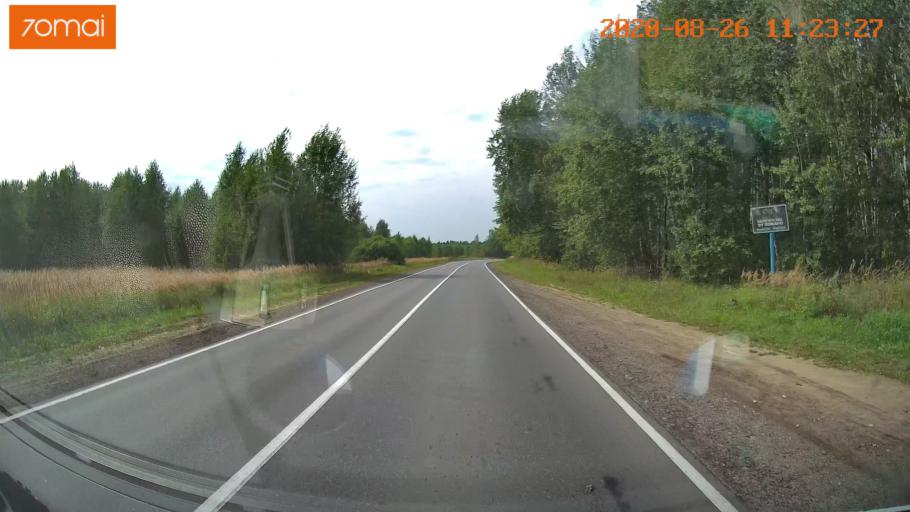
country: RU
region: Rjazan
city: Shilovo
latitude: 54.3520
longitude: 41.0103
